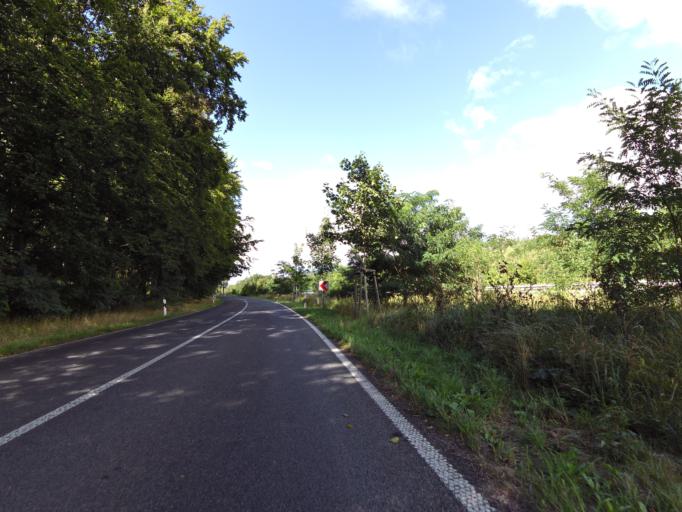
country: DE
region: Berlin
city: Marienfelde
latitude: 52.3707
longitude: 13.3594
